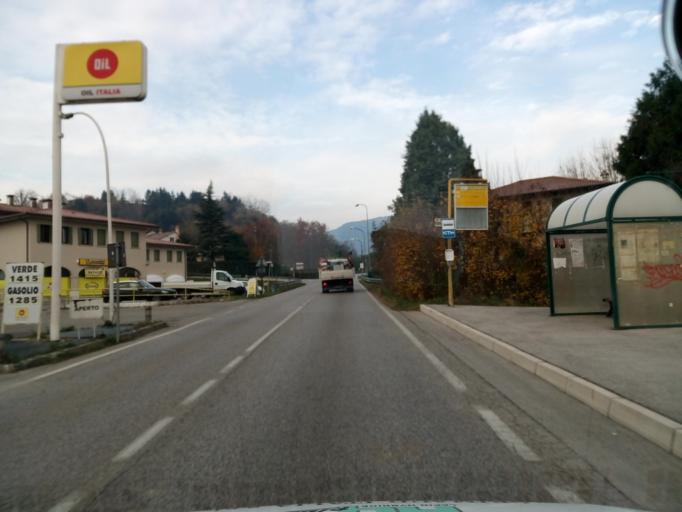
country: IT
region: Veneto
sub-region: Provincia di Treviso
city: Castelcucco
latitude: 45.8042
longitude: 11.8933
